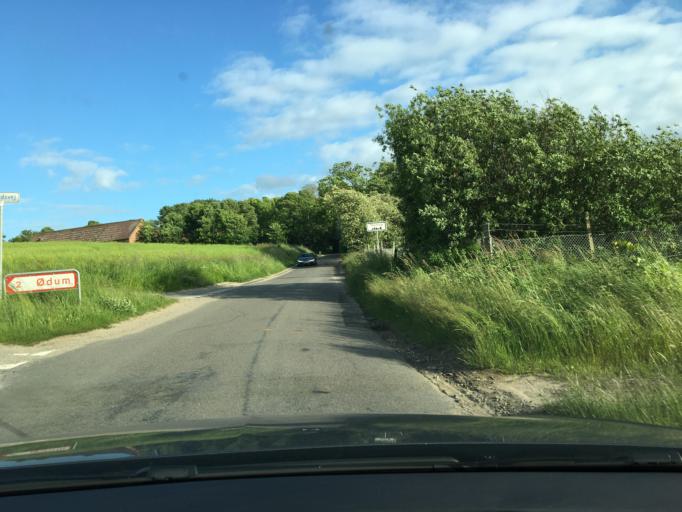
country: DK
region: Central Jutland
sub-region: Favrskov Kommune
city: Hinnerup
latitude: 56.3001
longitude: 10.1065
